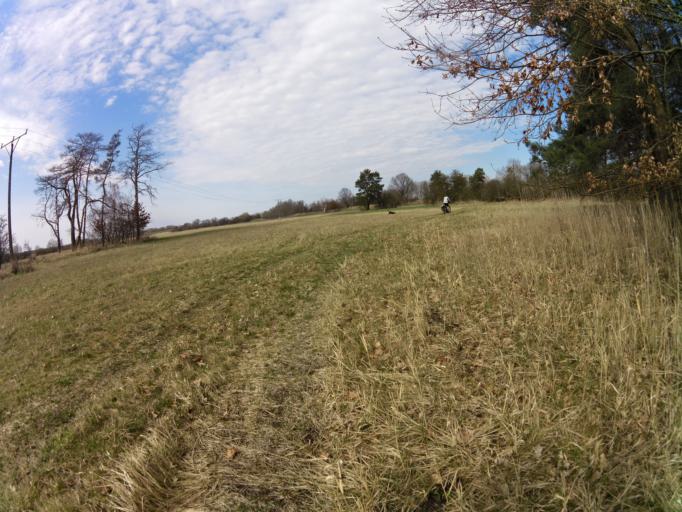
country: PL
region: West Pomeranian Voivodeship
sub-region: Powiat mysliborski
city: Mysliborz
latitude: 52.9686
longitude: 14.8813
